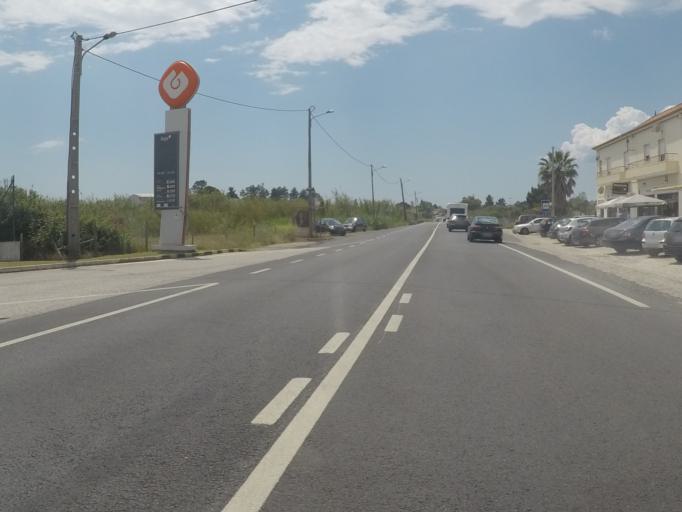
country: PT
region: Setubal
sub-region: Setubal
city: Setubal
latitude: 38.5497
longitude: -8.8116
